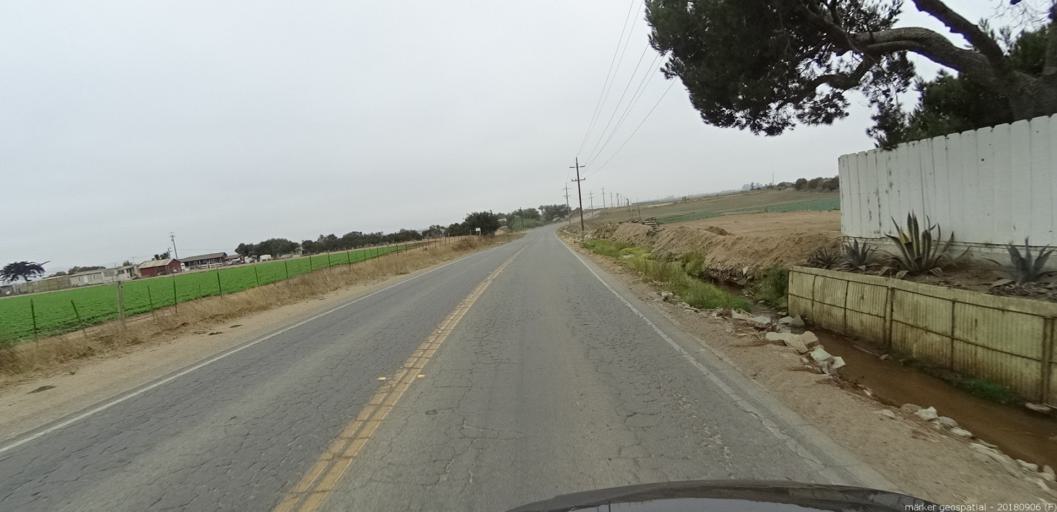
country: US
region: California
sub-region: Monterey County
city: Chualar
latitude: 36.6396
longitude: -121.5680
